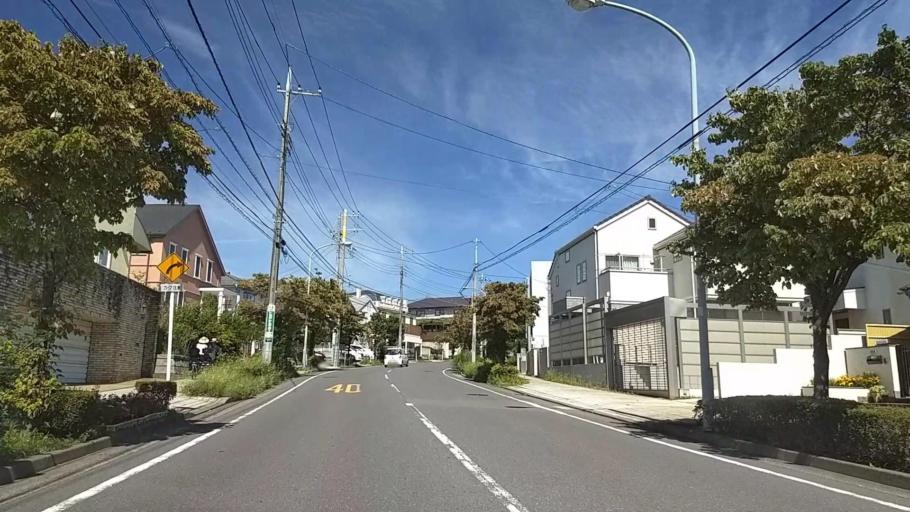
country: JP
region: Tokyo
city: Chofugaoka
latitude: 35.5622
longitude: 139.5497
